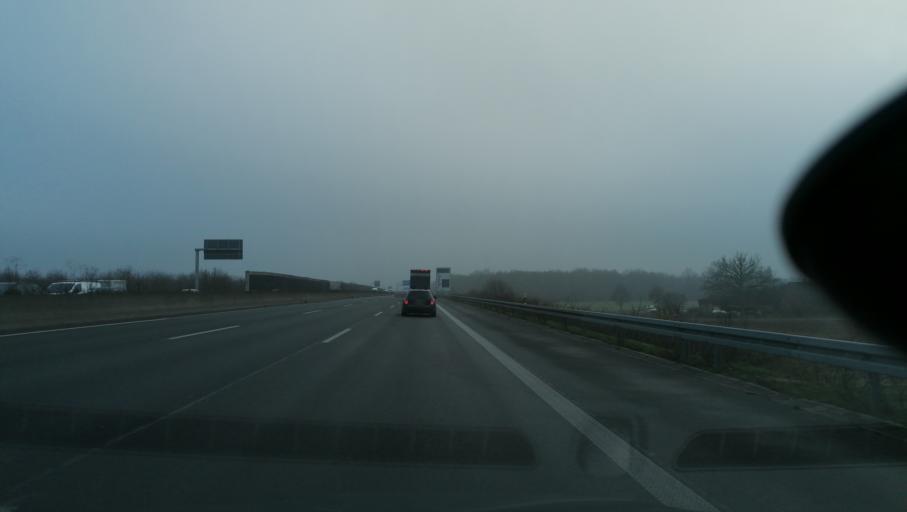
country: DE
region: North Rhine-Westphalia
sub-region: Regierungsbezirk Munster
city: Muenster
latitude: 51.9381
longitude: 7.5509
